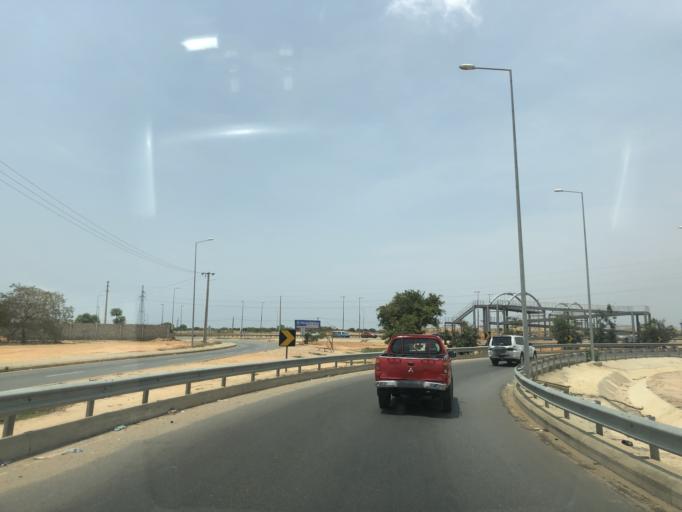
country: AO
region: Luanda
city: Luanda
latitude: -8.9747
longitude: 13.2524
